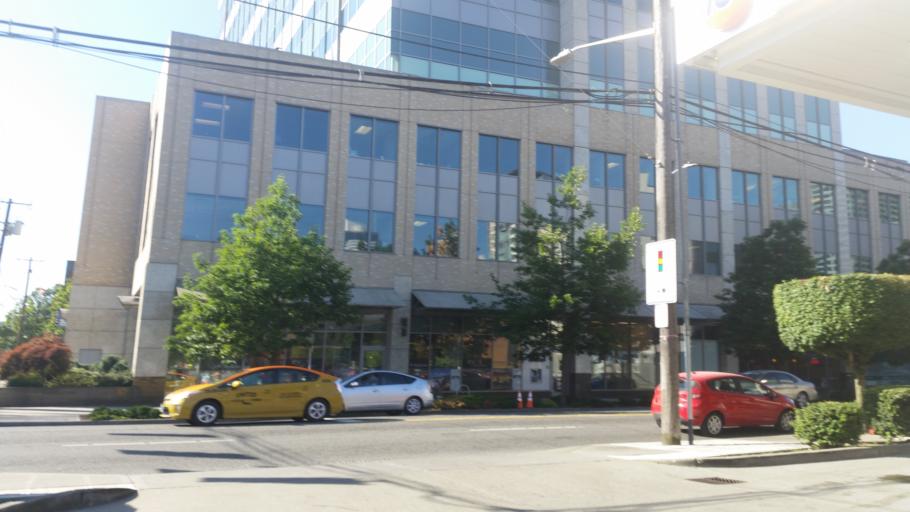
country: US
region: Washington
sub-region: King County
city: Seattle
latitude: 47.6062
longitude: -122.3239
